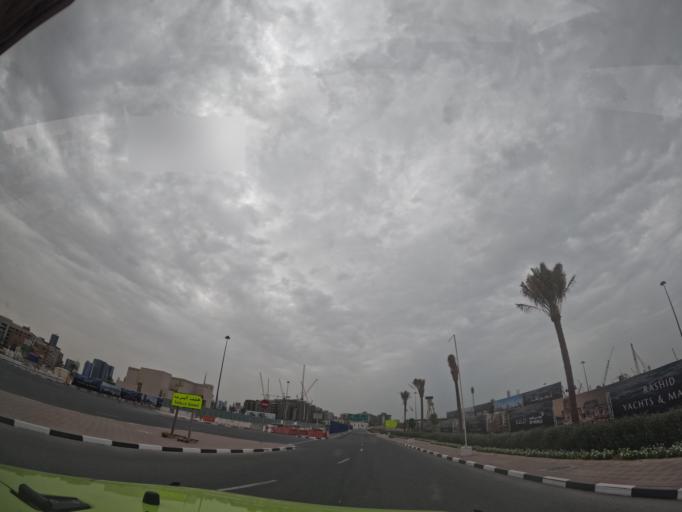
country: AE
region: Ash Shariqah
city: Sharjah
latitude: 25.2540
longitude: 55.2802
